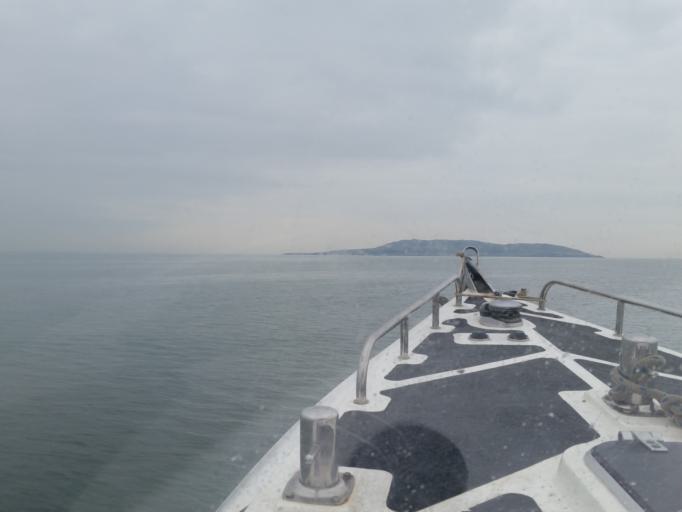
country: IE
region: Leinster
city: Portraine
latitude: 53.4680
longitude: -6.0855
